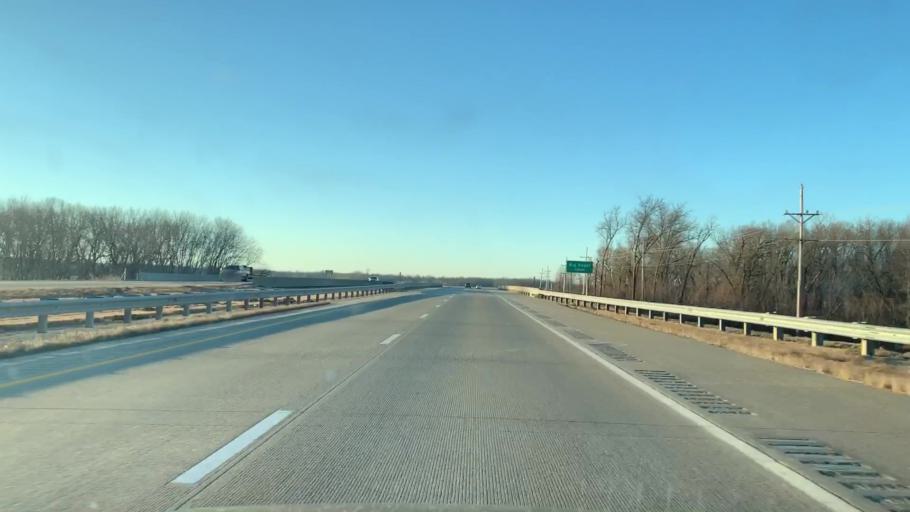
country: US
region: Kansas
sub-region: Linn County
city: Pleasanton
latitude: 38.2372
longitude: -94.6908
